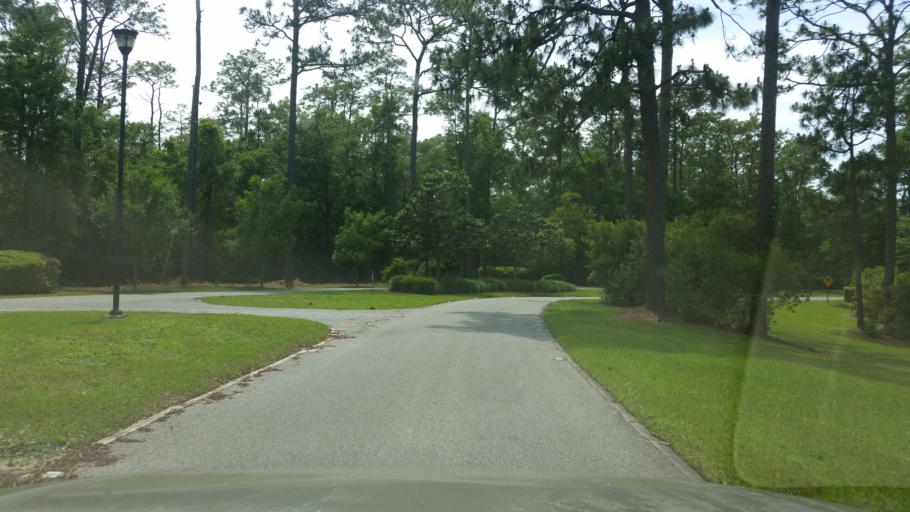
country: US
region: Florida
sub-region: Escambia County
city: Ferry Pass
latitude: 30.5389
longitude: -87.2094
